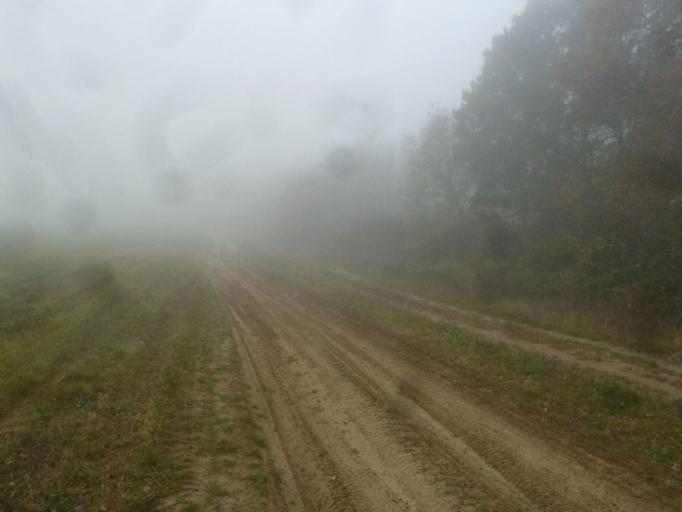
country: HU
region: Zala
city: Nagykanizsa
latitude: 46.5641
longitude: 17.0223
